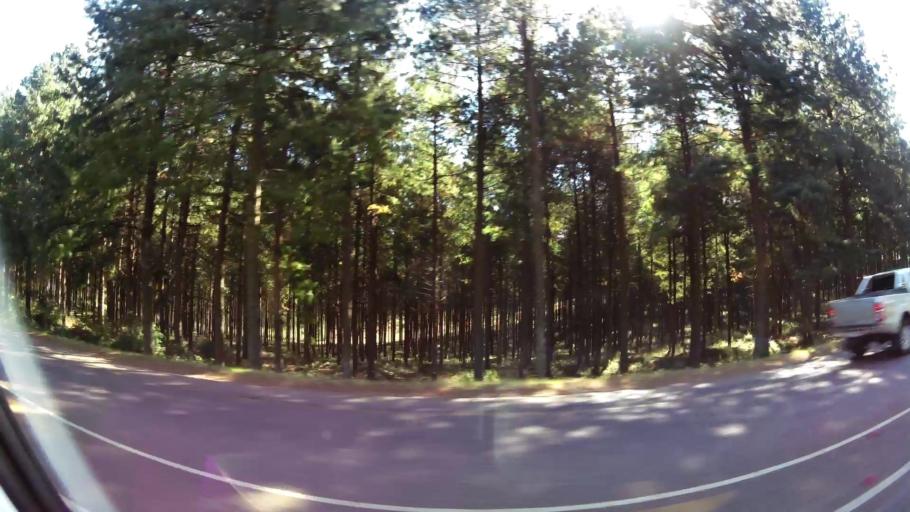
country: ZA
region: Limpopo
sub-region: Capricorn District Municipality
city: Mankoeng
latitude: -23.9267
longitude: 29.9611
